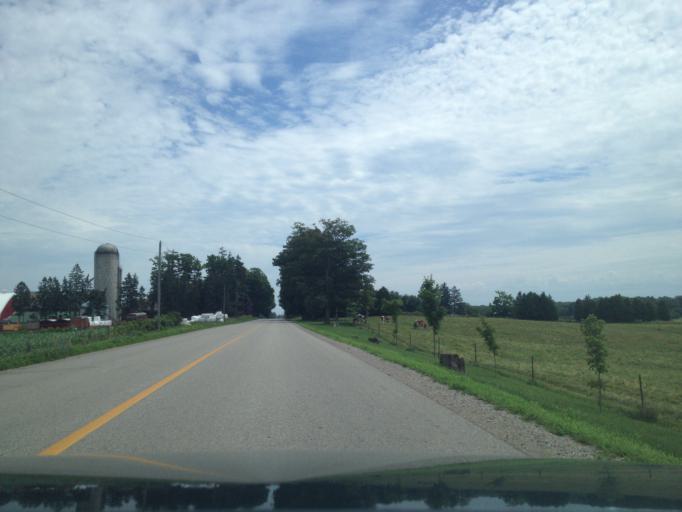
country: CA
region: Ontario
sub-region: Oxford County
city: Woodstock
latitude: 42.9913
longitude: -80.6704
